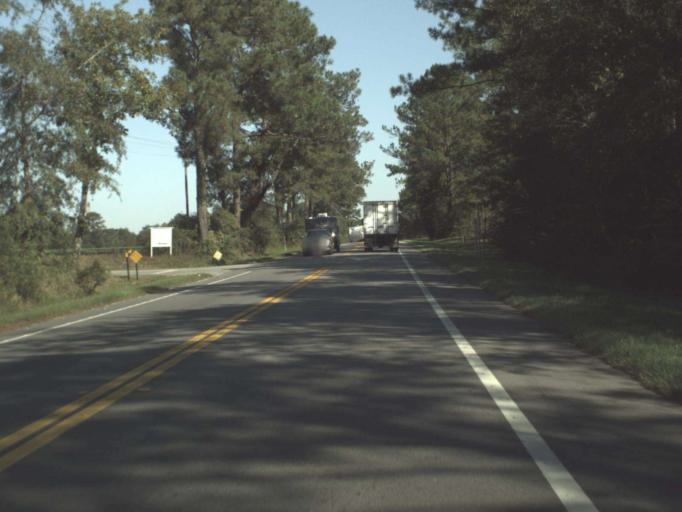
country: US
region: Alabama
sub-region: Covington County
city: Florala
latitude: 30.9672
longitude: -86.3729
